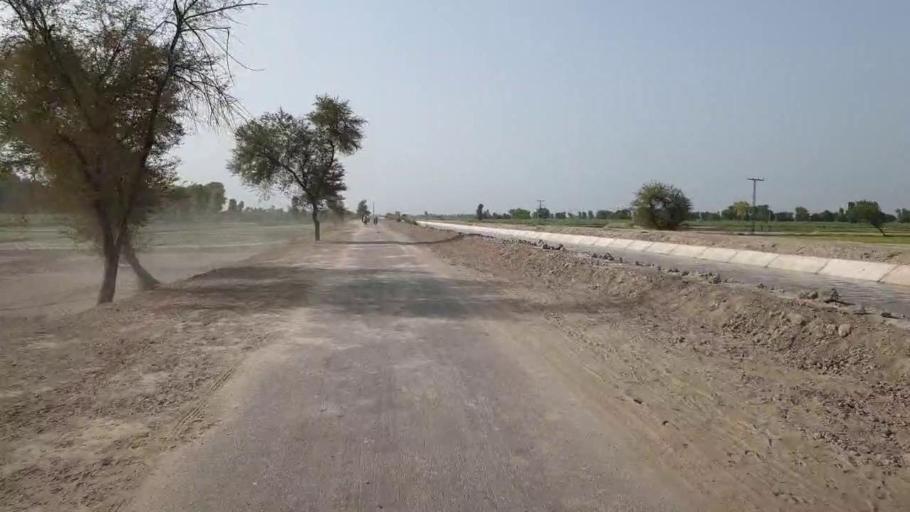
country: PK
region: Sindh
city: Daur
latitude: 26.3340
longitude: 68.1642
